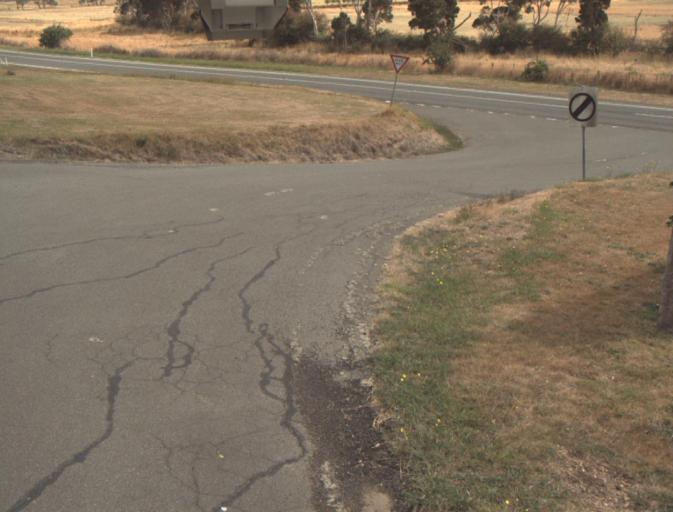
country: AU
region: Tasmania
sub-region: Launceston
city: Mayfield
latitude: -41.3262
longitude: 147.0651
